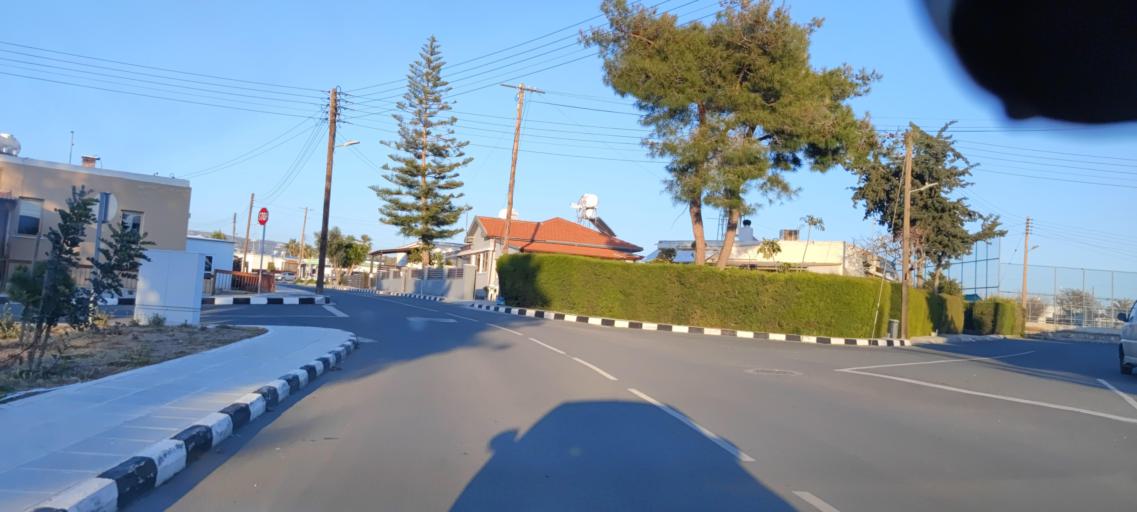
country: CY
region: Pafos
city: Paphos
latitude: 34.7830
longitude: 32.4150
